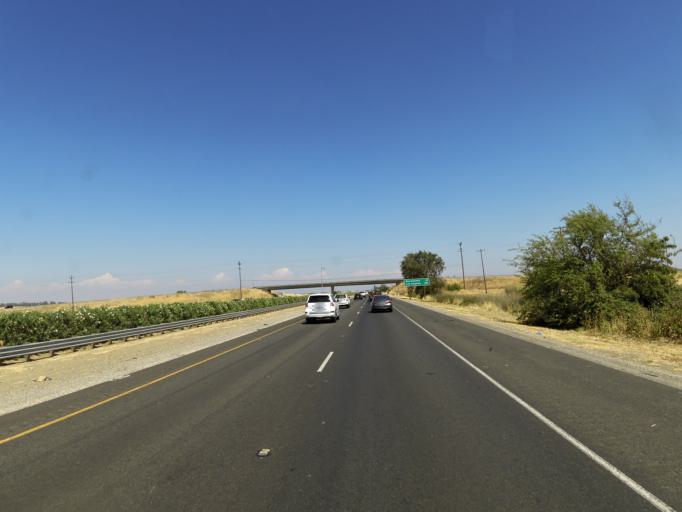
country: US
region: California
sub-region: Yolo County
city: West Sacramento
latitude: 38.6711
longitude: -121.5791
